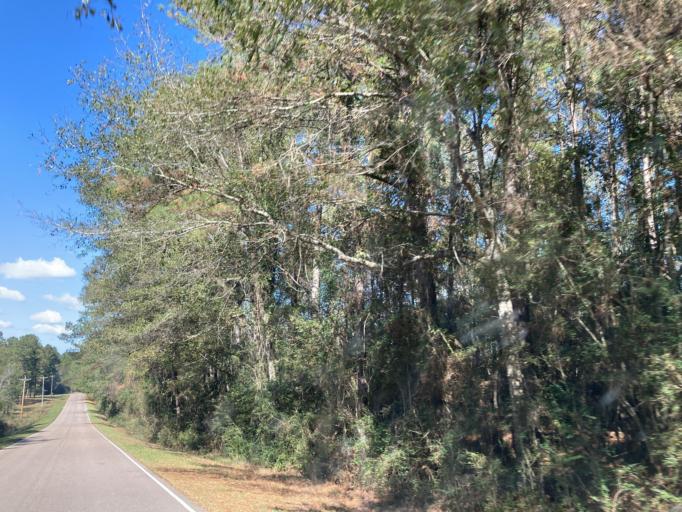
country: US
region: Mississippi
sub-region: Lamar County
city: Sumrall
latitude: 31.3072
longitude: -89.5410
